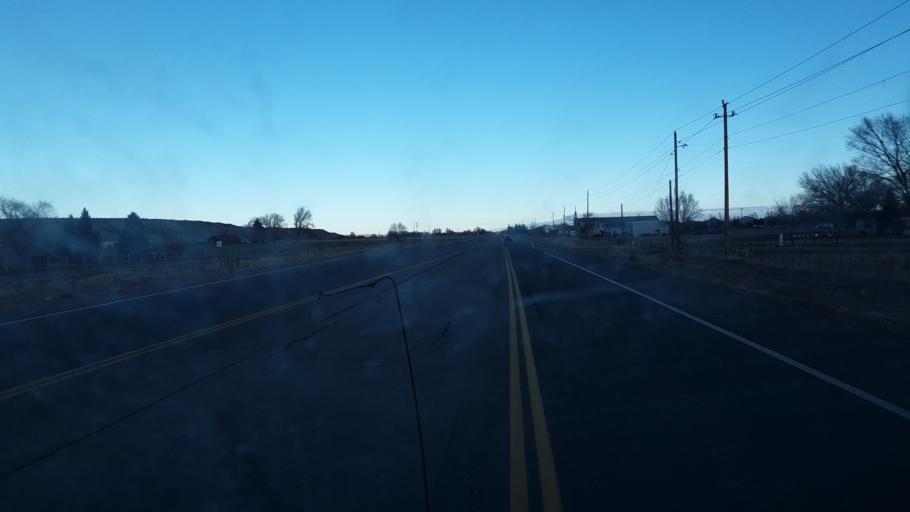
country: US
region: Colorado
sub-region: Montrose County
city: Montrose
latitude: 38.3752
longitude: -107.8161
